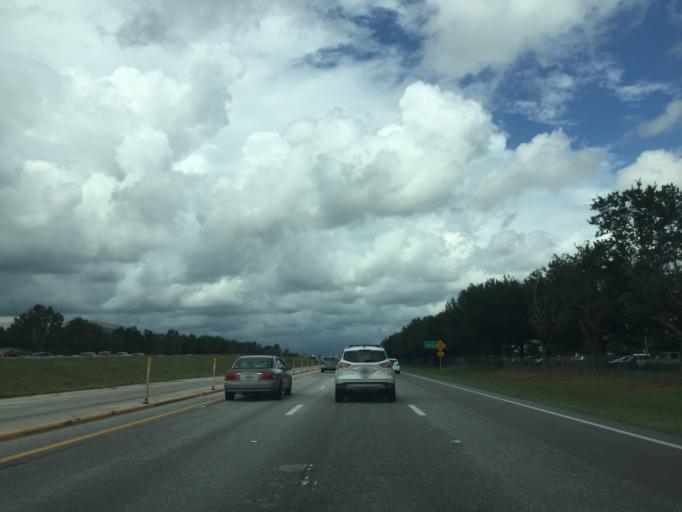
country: US
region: Florida
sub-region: Orange County
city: Eatonville
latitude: 28.6331
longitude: -81.3993
